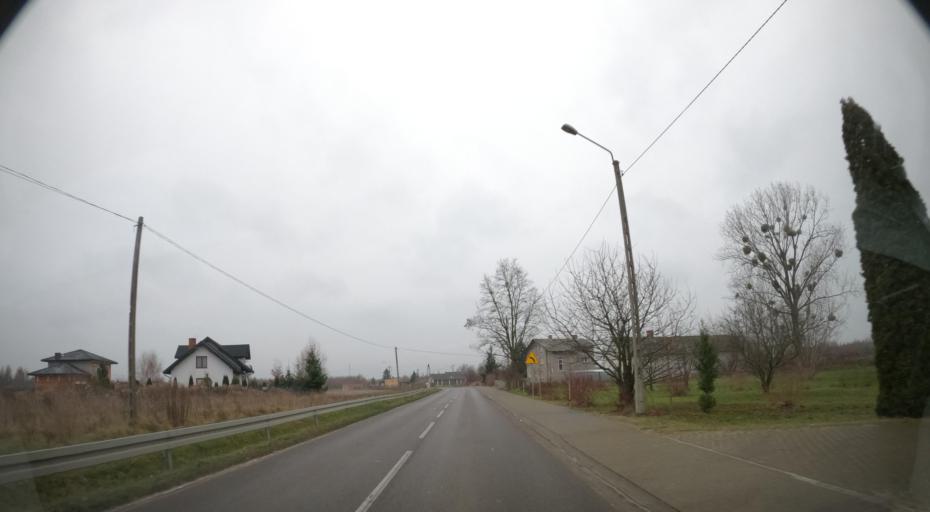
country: PL
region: Masovian Voivodeship
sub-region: Powiat radomski
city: Skaryszew
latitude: 51.3850
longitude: 21.2560
